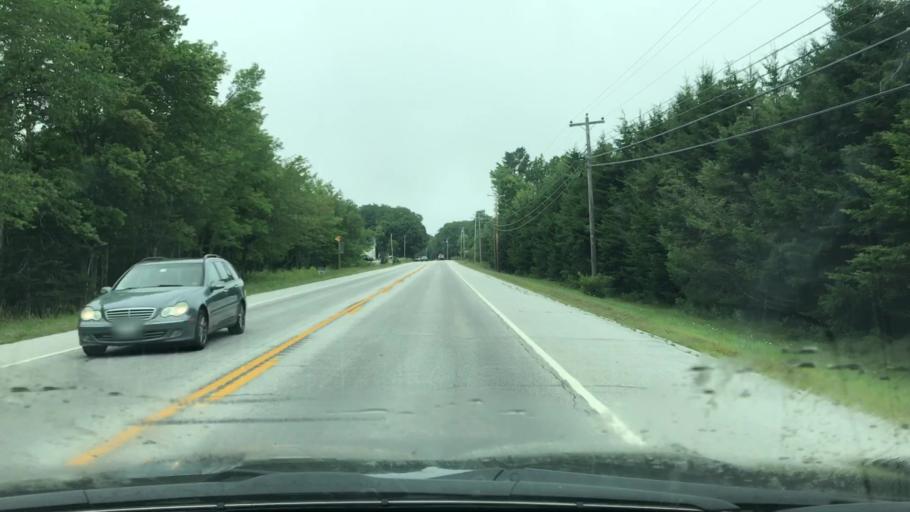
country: US
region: Maine
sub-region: Waldo County
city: Northport
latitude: 44.3270
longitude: -68.9597
